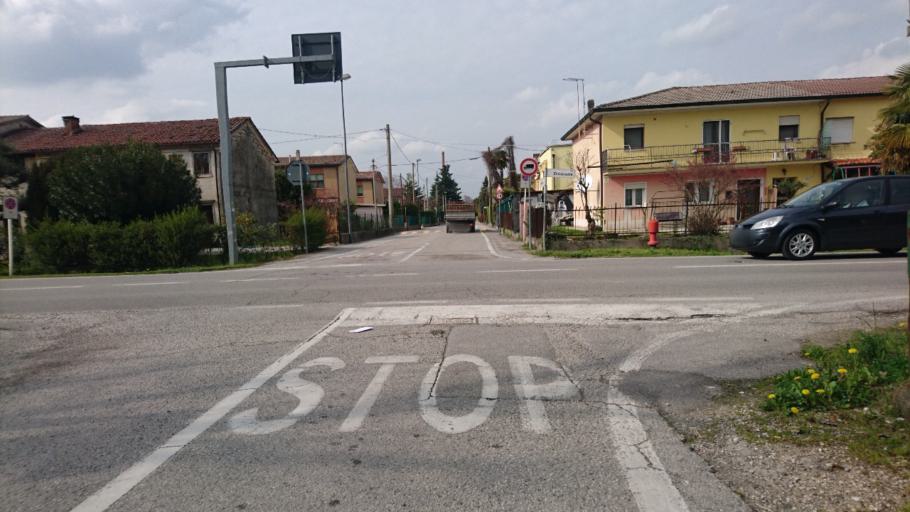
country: IT
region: Veneto
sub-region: Provincia di Padova
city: Piazzola sul Brenta
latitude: 45.5385
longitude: 11.7907
